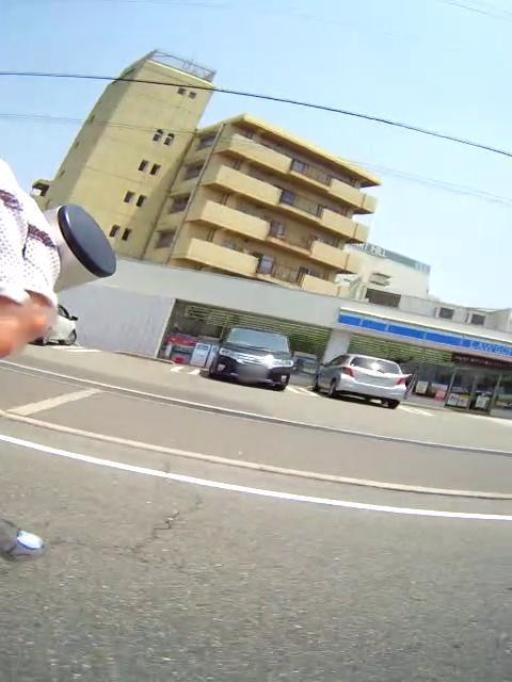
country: JP
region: Osaka
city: Mino
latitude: 34.8273
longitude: 135.4889
